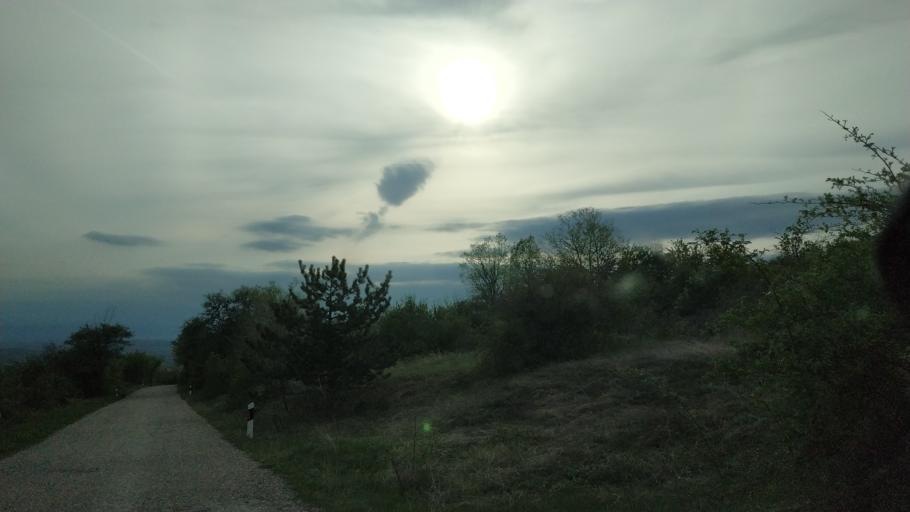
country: RS
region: Central Serbia
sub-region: Zajecarski Okrug
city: Soko Banja
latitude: 43.5337
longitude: 21.8778
